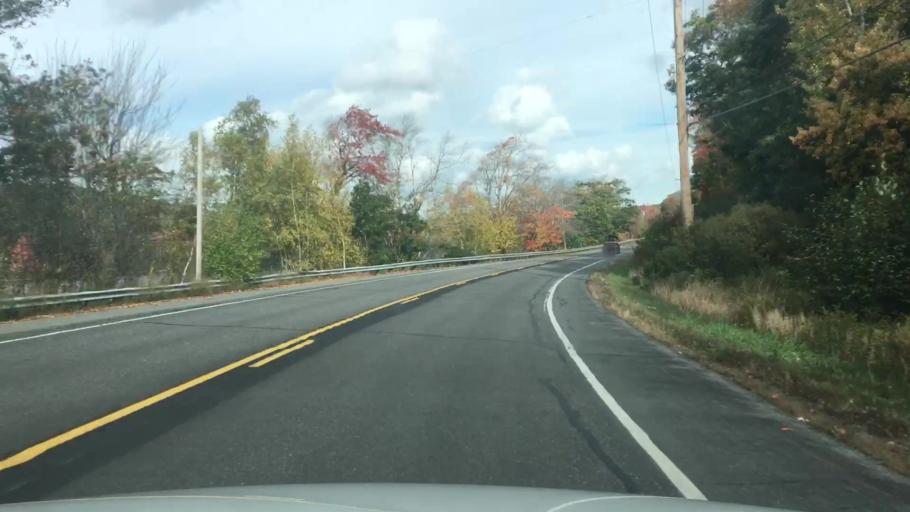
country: US
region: Maine
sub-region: Knox County
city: Rockport
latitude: 44.1664
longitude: -69.1196
